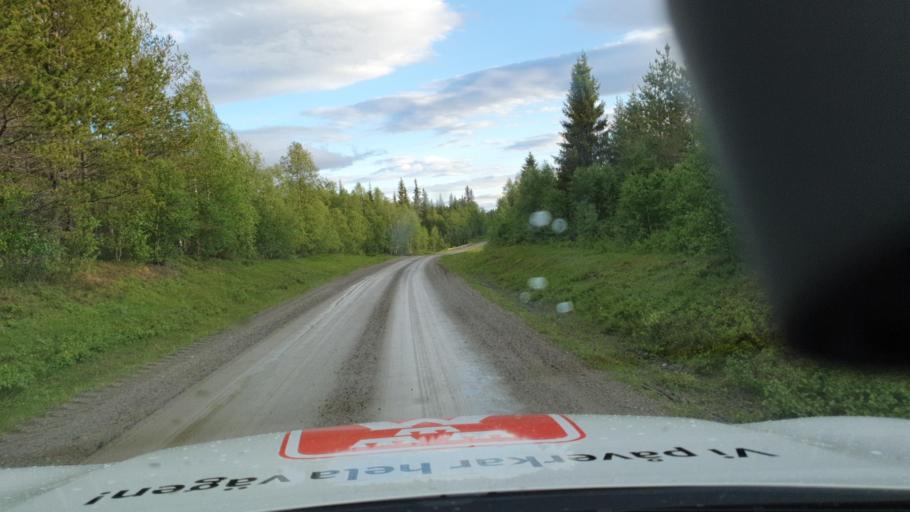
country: SE
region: Vaesterbotten
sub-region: Storumans Kommun
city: Storuman
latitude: 64.7468
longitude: 17.0813
